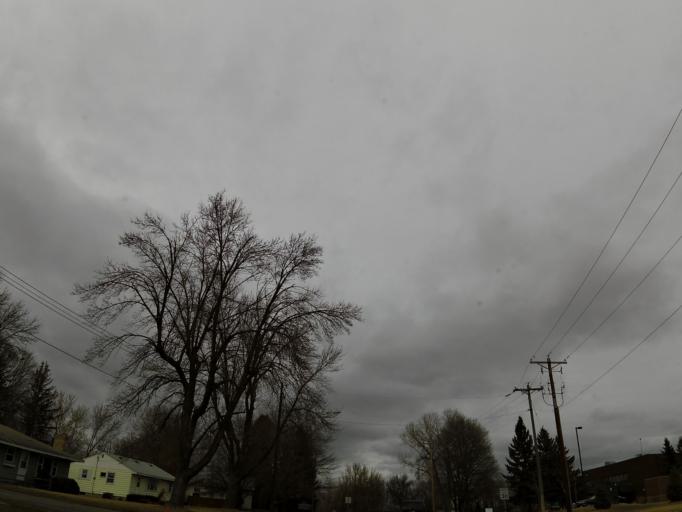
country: US
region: Minnesota
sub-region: Scott County
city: Prior Lake
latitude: 44.7075
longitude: -93.4305
